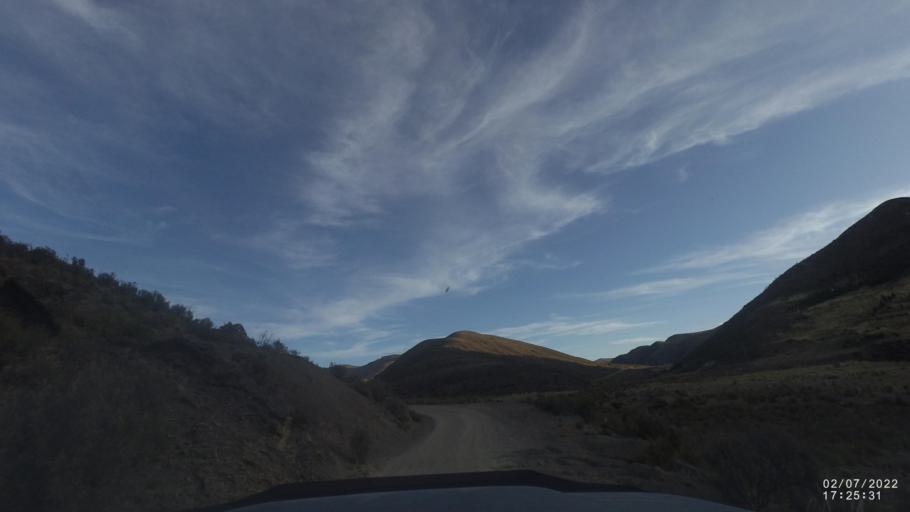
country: BO
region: Cochabamba
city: Irpa Irpa
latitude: -17.8768
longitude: -66.6078
